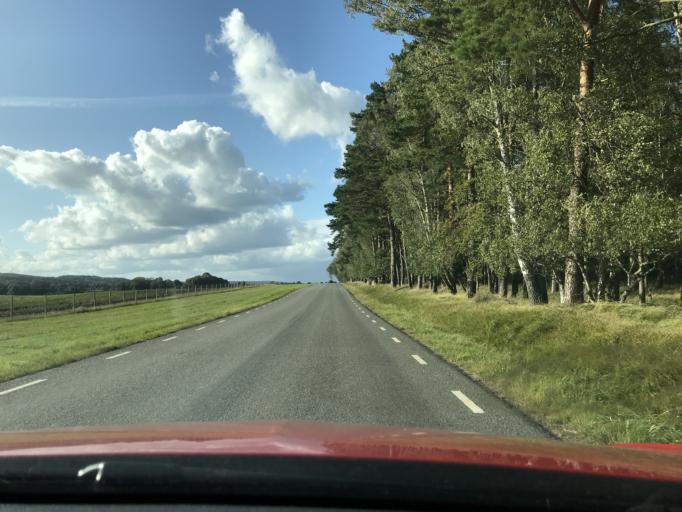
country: SE
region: Skane
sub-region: Kristianstads Kommun
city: Degeberga
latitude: 55.8590
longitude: 14.0667
